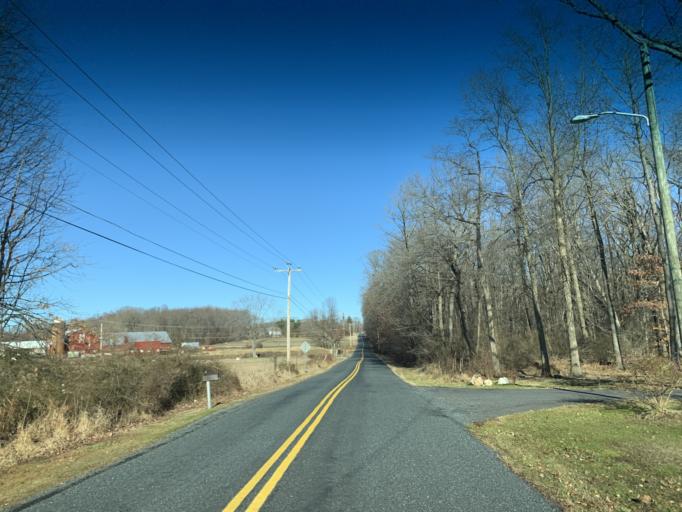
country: US
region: Maryland
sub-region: Harford County
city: Riverside
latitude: 39.5364
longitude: -76.2394
